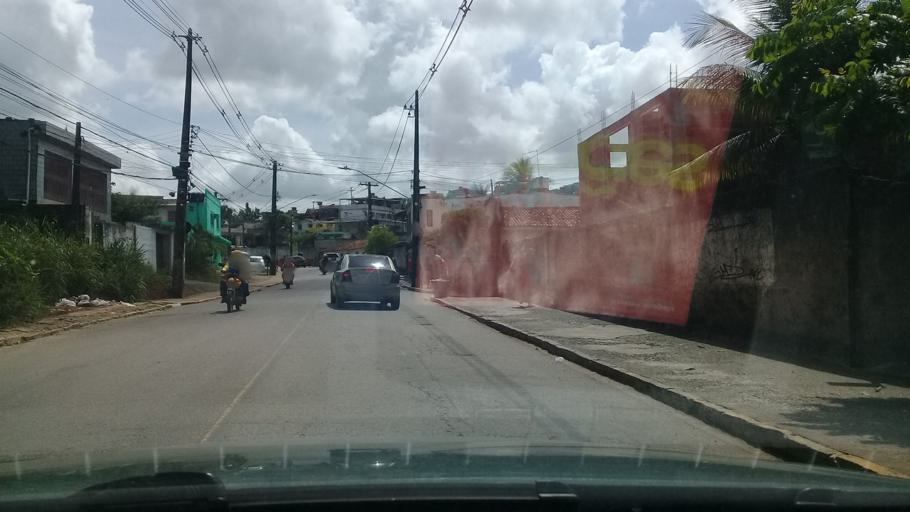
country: BR
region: Pernambuco
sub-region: Jaboatao Dos Guararapes
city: Jaboatao dos Guararapes
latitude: -8.1027
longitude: -35.0188
